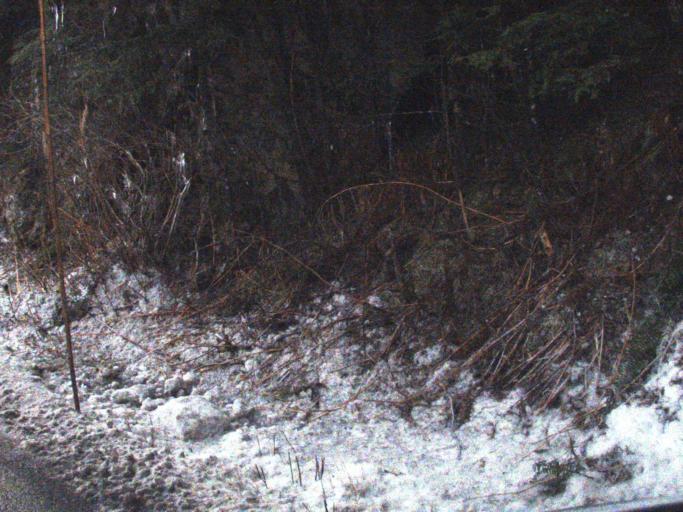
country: CA
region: British Columbia
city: Agassiz
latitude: 48.9006
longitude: -121.6892
